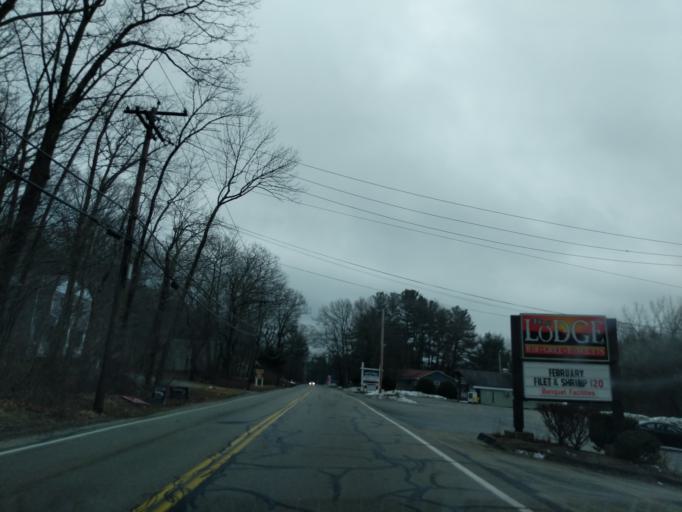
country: US
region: Massachusetts
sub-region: Worcester County
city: Webster
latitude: 42.0570
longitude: -71.8427
